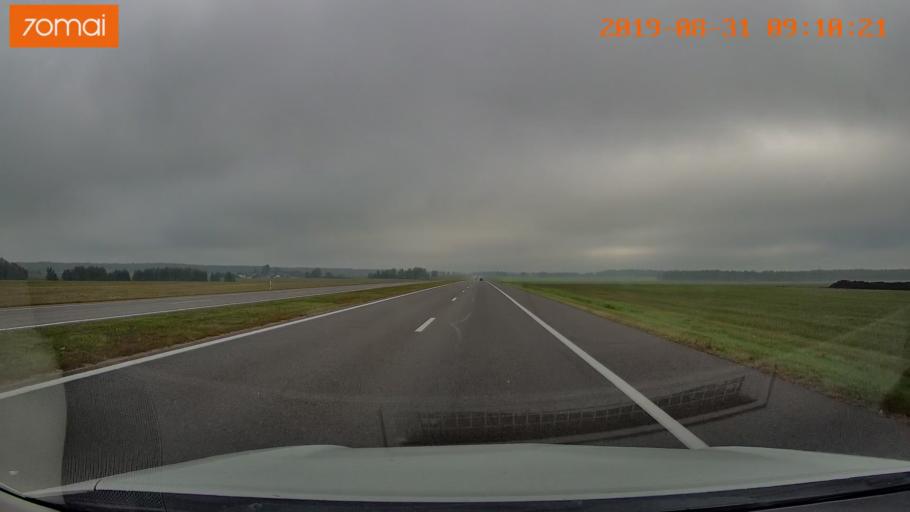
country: BY
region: Minsk
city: Chervyen'
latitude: 53.7380
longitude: 28.5264
